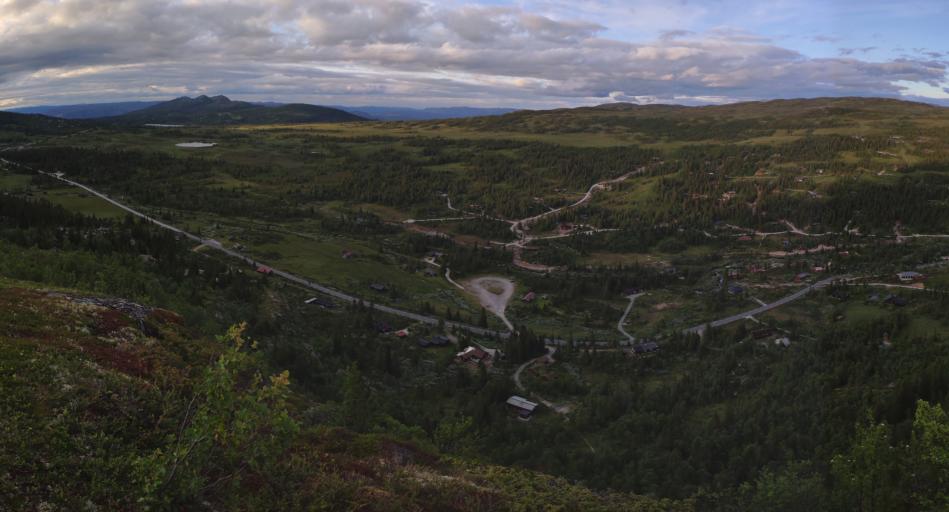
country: NO
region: Buskerud
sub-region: Nes
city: Nesbyen
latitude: 60.3599
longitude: 9.1836
